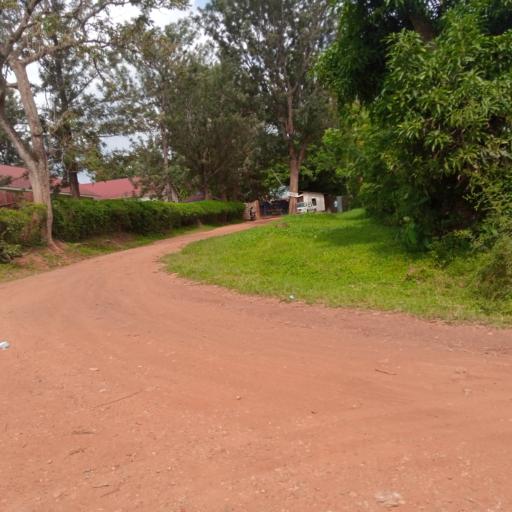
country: UG
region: Eastern Region
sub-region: Mbale District
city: Mbale
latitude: 1.0928
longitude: 34.1877
